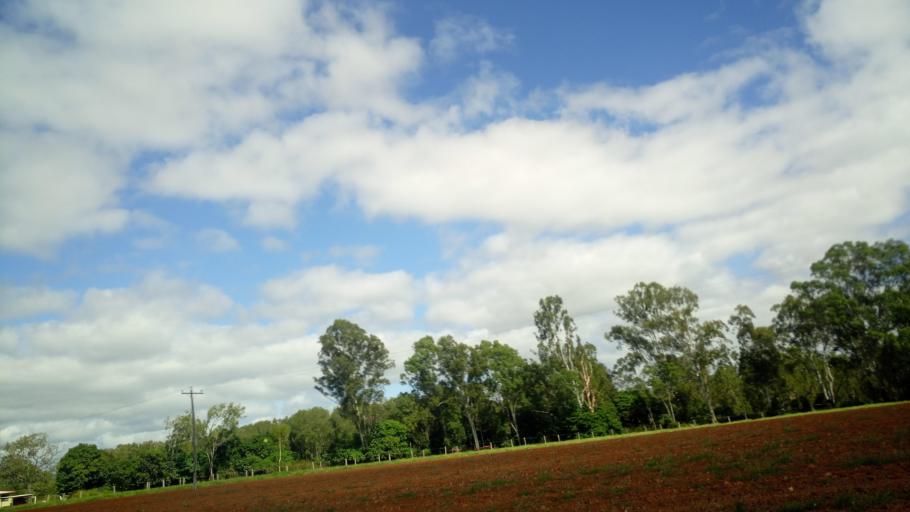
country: AU
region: Queensland
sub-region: Tablelands
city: Mareeba
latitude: -16.9766
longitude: 145.4670
